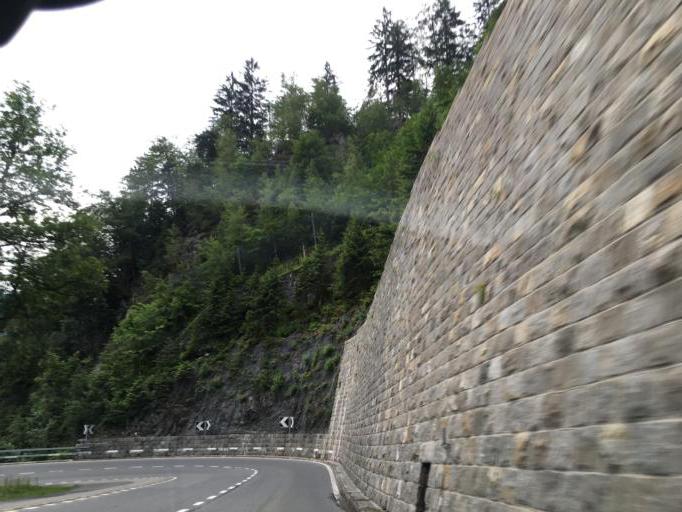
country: CH
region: Obwalden
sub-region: Obwalden
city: Engelberg
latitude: 46.8407
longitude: 8.3772
